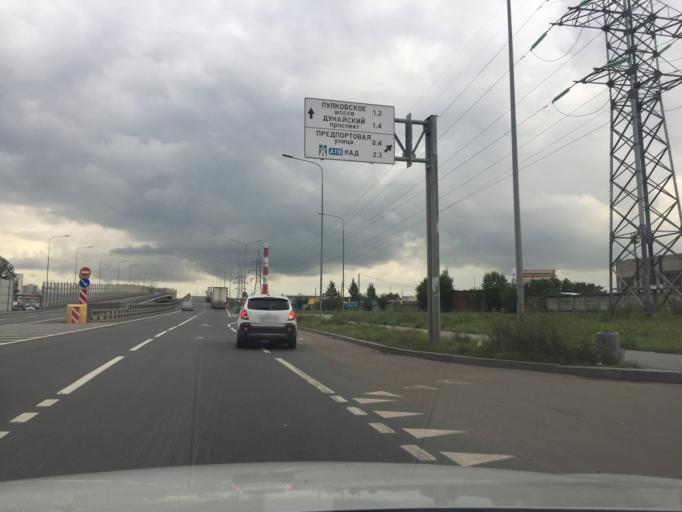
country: RU
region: St.-Petersburg
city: Dachnoye
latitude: 59.8354
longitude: 30.3058
